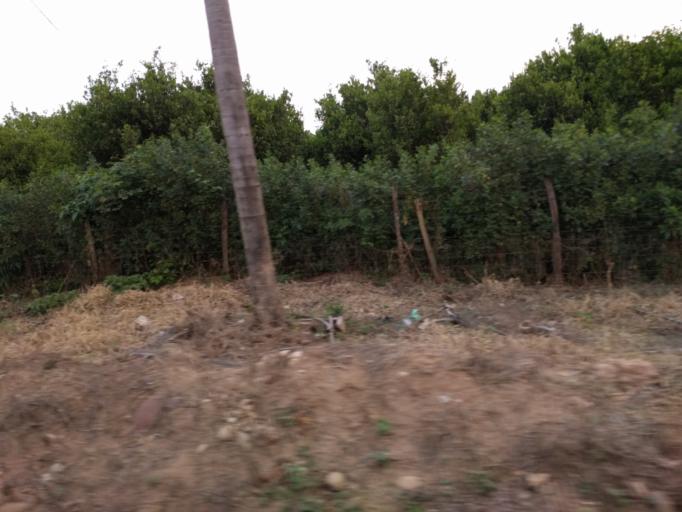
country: BO
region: Santa Cruz
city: Santa Rita
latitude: -17.9461
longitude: -63.3569
